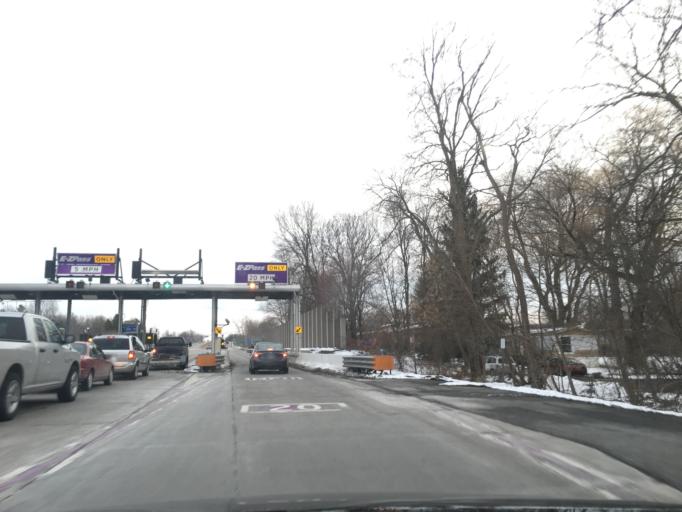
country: US
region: New York
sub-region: Ontario County
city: Victor
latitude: 42.9917
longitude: -77.3659
